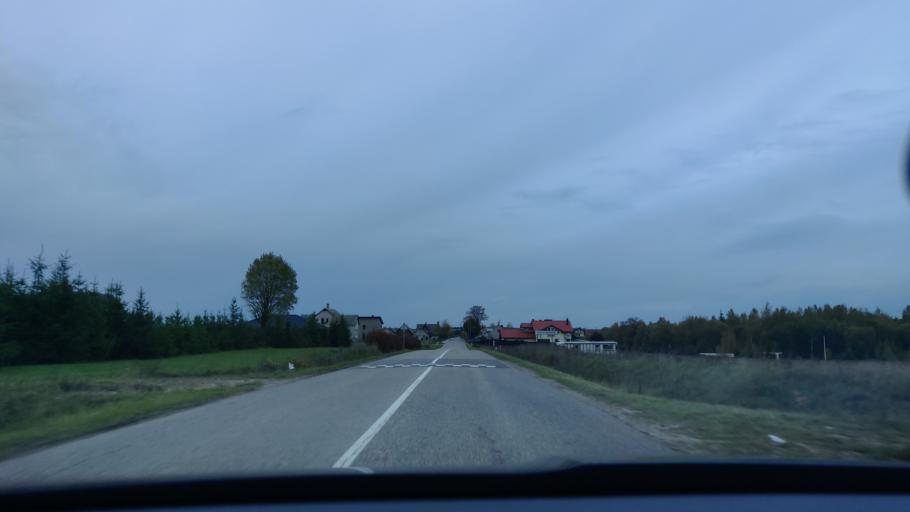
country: LT
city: Lentvaris
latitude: 54.5784
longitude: 25.0517
